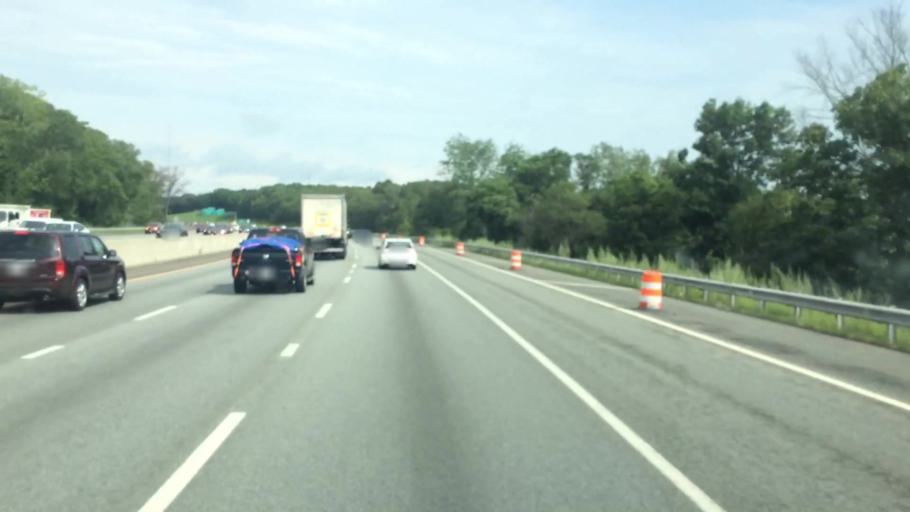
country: US
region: Massachusetts
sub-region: Norfolk County
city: Needham
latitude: 42.2784
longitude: -71.1998
